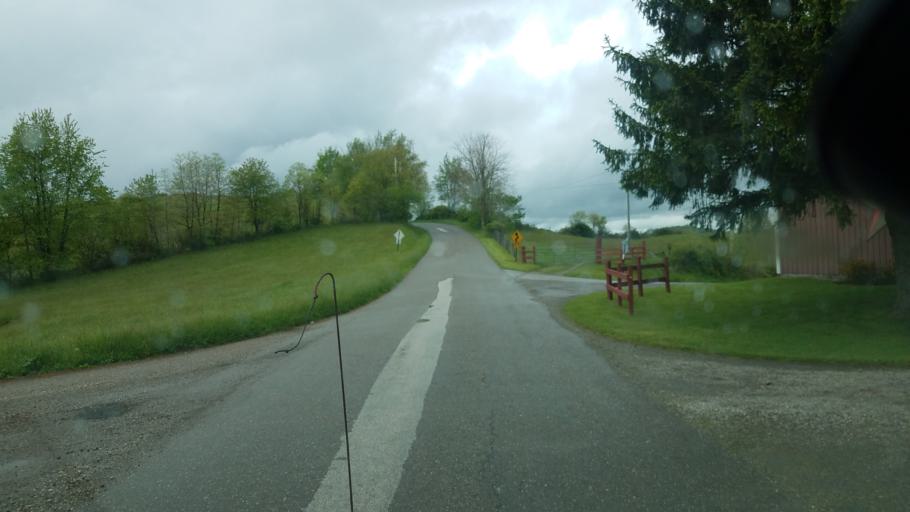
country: US
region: Ohio
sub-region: Tuscarawas County
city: Rockford
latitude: 40.4002
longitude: -81.1923
